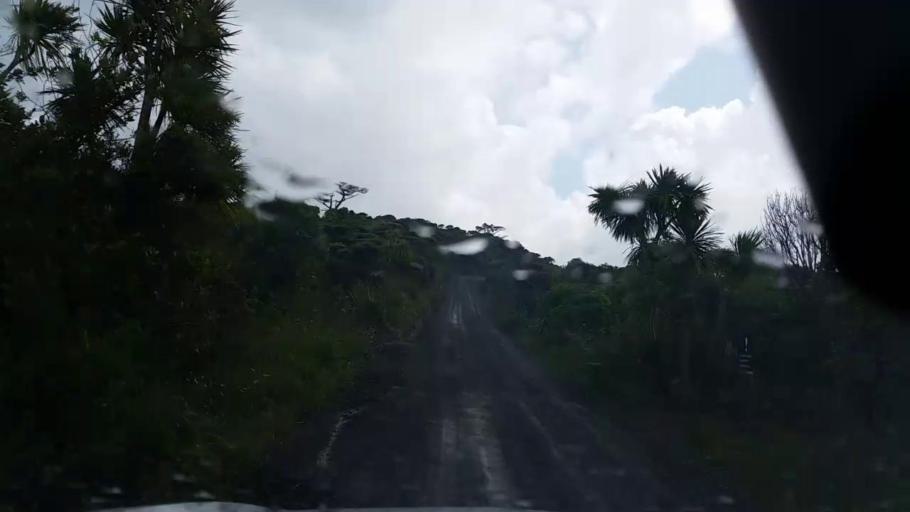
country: NZ
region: Auckland
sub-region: Auckland
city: Muriwai Beach
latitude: -36.9306
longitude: 174.4669
